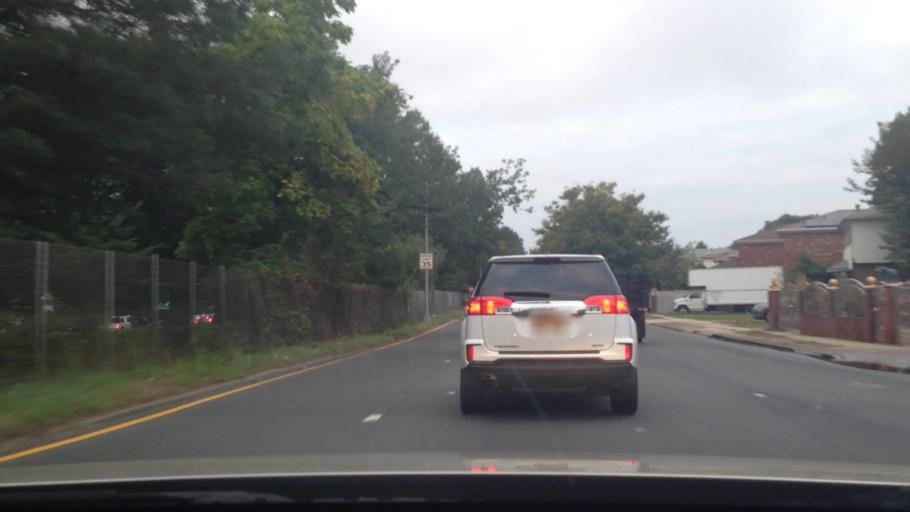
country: US
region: New York
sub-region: Nassau County
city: South Valley Stream
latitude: 40.6665
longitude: -73.7587
